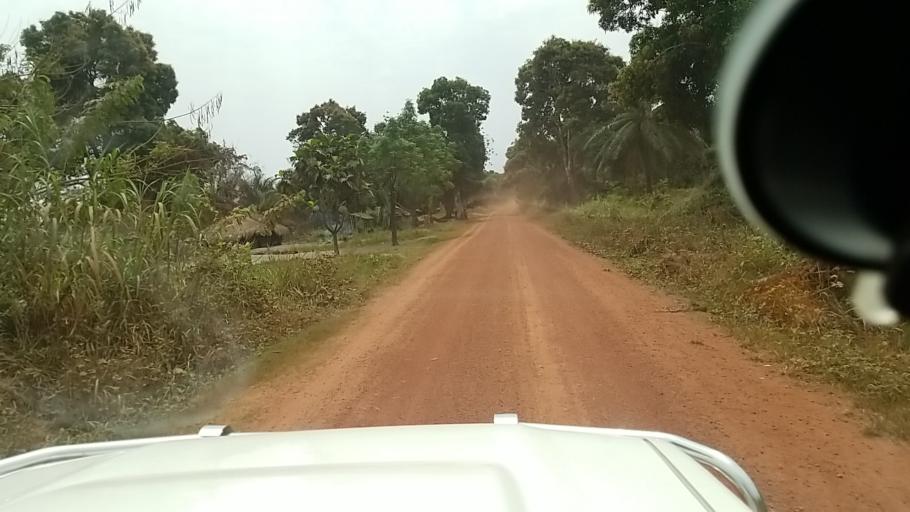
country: CD
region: Equateur
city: Libenge
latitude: 3.7413
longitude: 18.7823
